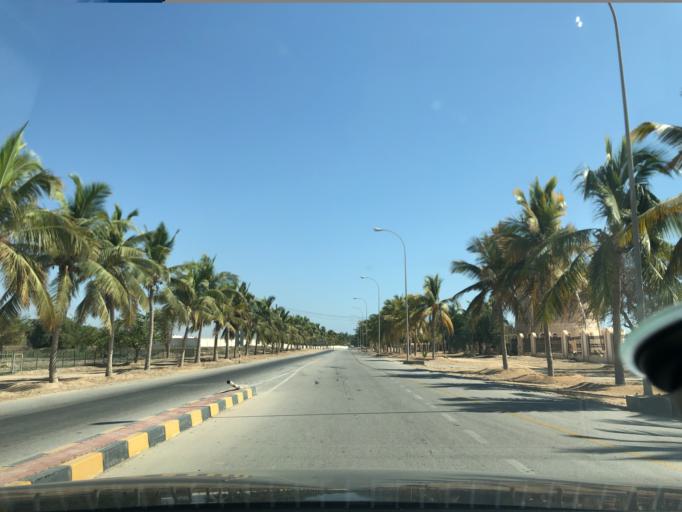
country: OM
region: Zufar
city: Salalah
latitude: 17.0397
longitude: 54.3747
